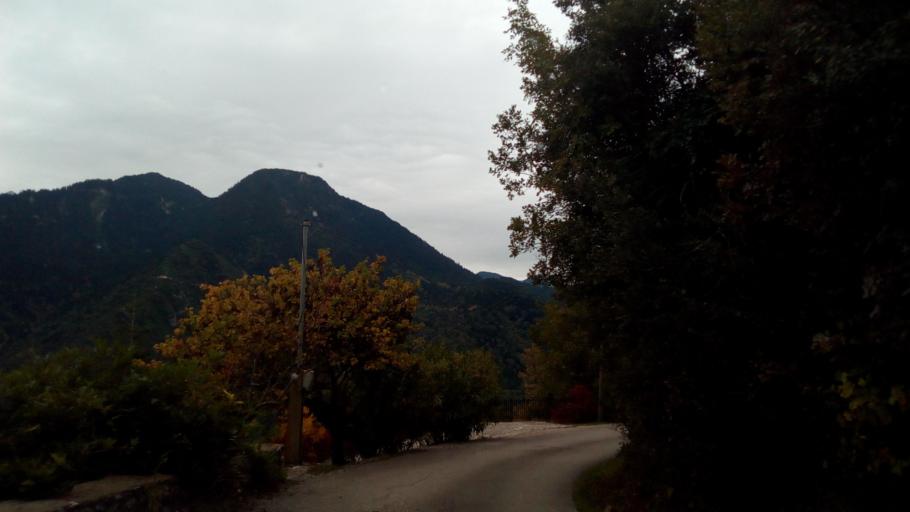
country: GR
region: West Greece
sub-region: Nomos Aitolias kai Akarnanias
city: Thermo
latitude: 38.6051
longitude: 21.8491
